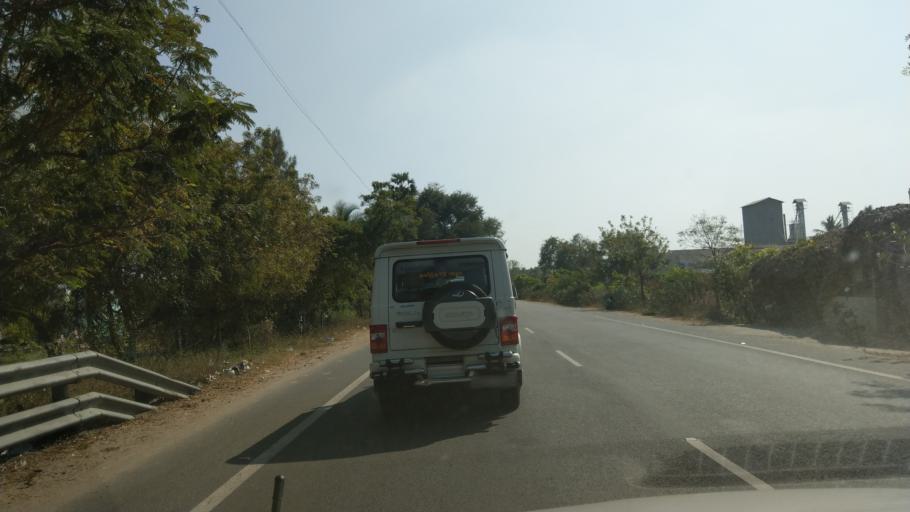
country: IN
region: Tamil Nadu
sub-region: Vellore
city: Arcot
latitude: 12.8849
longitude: 79.3181
